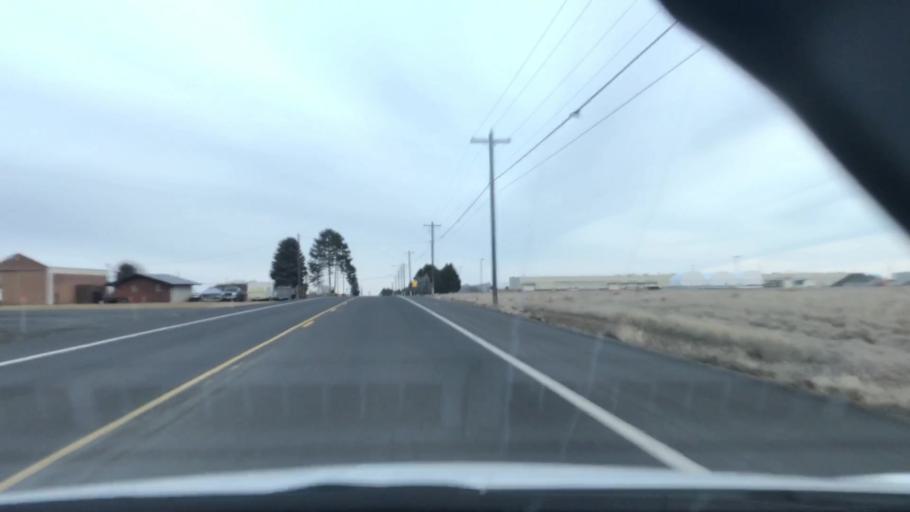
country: US
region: Washington
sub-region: Grant County
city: Moses Lake
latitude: 47.1467
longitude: -119.2468
